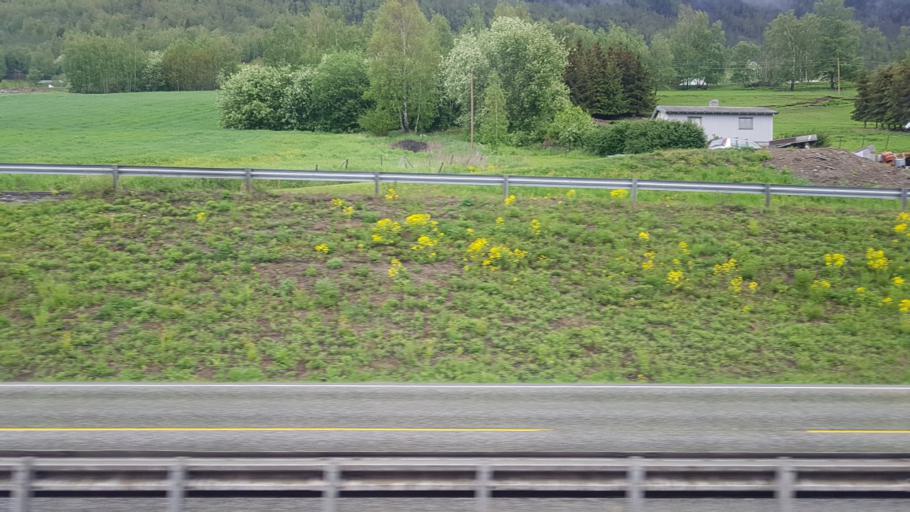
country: NO
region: Oppland
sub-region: Nord-Fron
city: Vinstra
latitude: 61.6663
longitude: 9.6671
